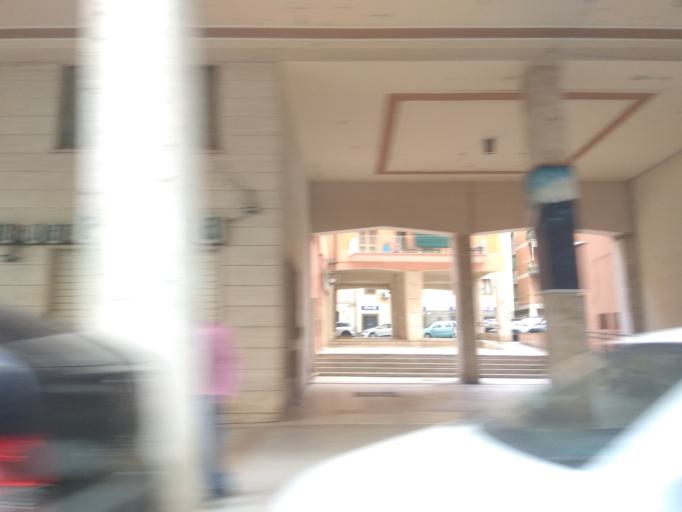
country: IT
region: Latium
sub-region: Citta metropolitana di Roma Capitale
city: Civitavecchia
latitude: 42.0938
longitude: 11.7907
